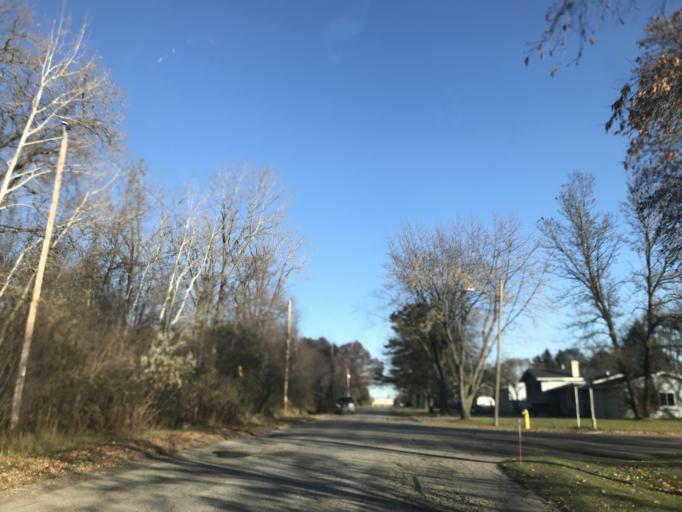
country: US
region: Wisconsin
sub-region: Marinette County
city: Peshtigo
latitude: 45.0595
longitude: -87.7422
